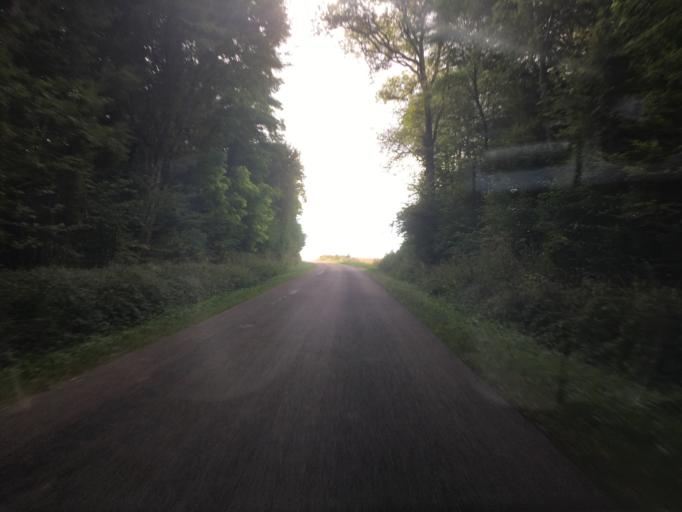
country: FR
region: Bourgogne
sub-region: Departement de l'Yonne
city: Fleury-la-Vallee
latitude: 47.8862
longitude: 3.4554
